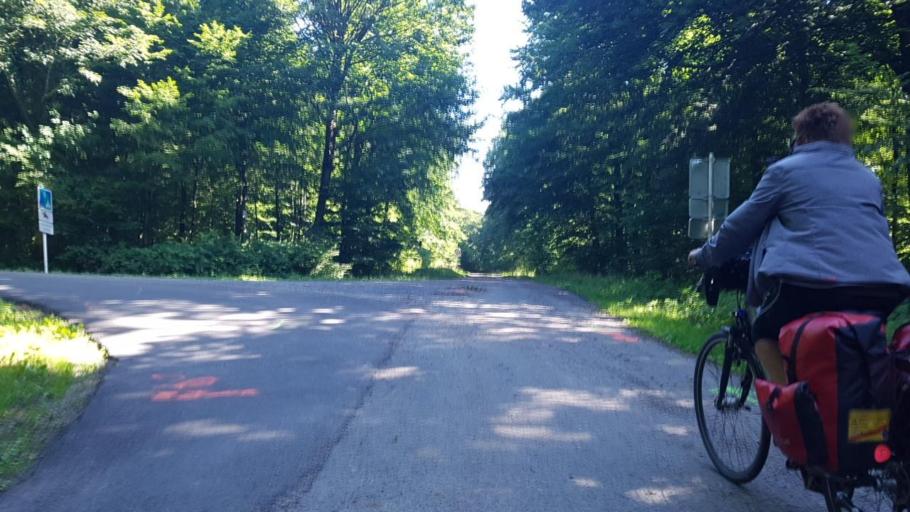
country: FR
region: Nord-Pas-de-Calais
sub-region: Departement du Nord
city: Anor
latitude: 49.9670
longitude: 4.1151
